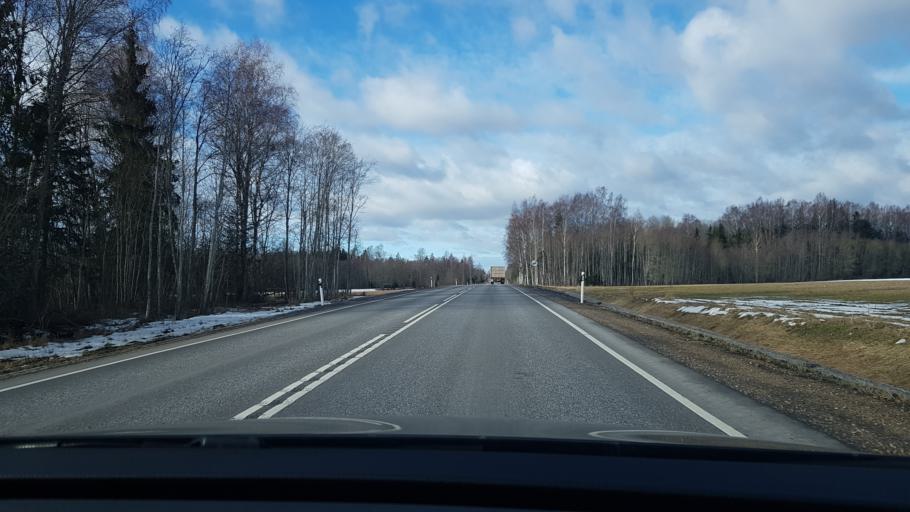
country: EE
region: Viljandimaa
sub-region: Moisakuela linn
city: Moisakula
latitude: 58.1418
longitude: 25.0941
